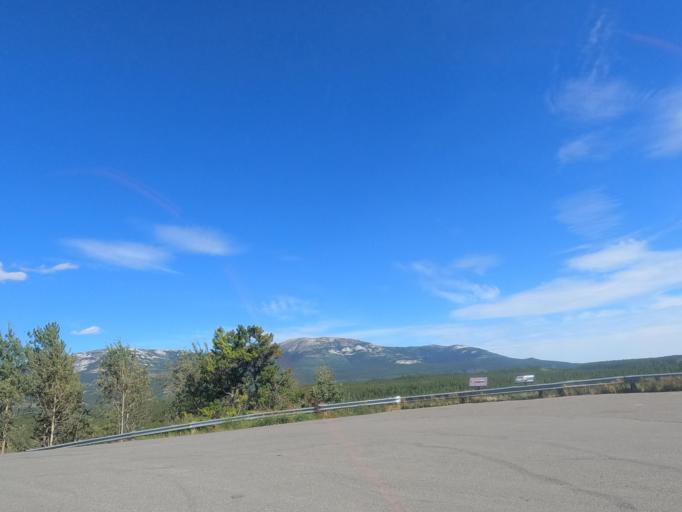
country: CA
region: Yukon
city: Whitehorse
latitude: 60.6670
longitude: -135.0325
